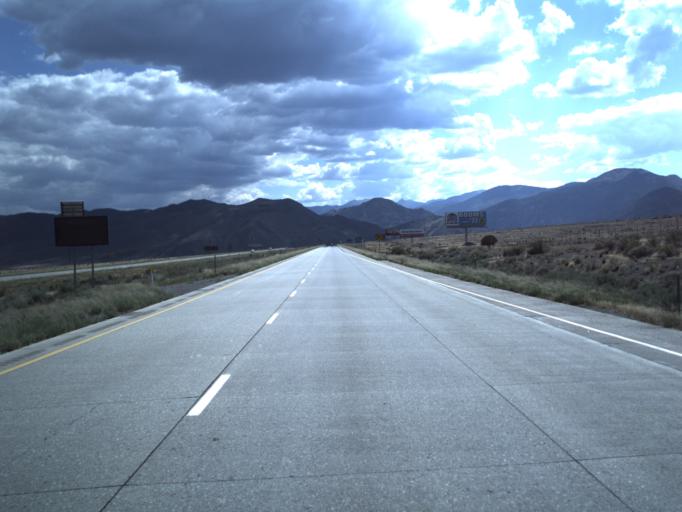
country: US
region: Utah
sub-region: Sevier County
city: Monroe
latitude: 38.6168
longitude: -112.2299
